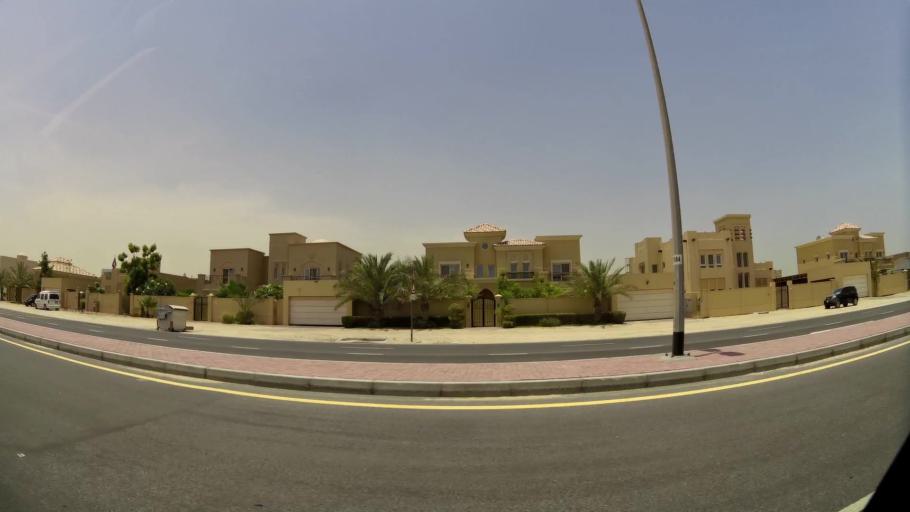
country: AE
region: Dubai
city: Dubai
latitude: 25.0873
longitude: 55.2375
